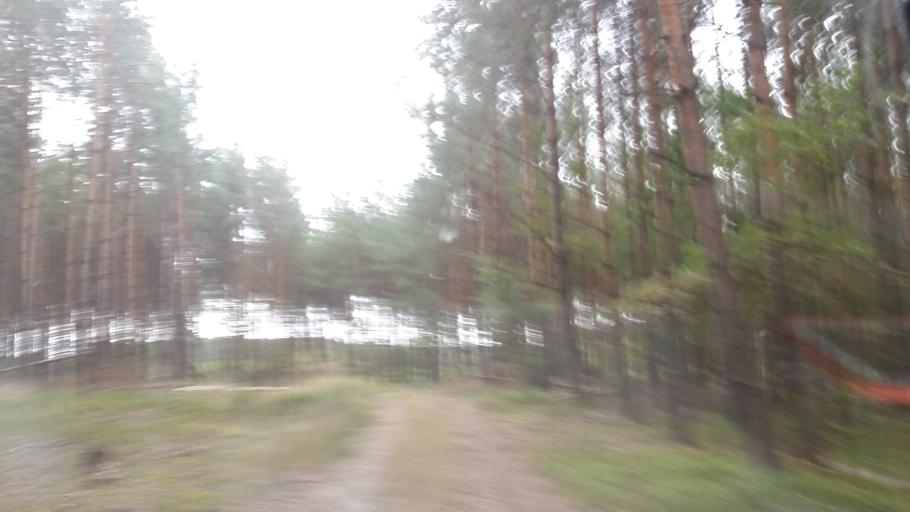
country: PL
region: West Pomeranian Voivodeship
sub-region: Powiat choszczenski
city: Bierzwnik
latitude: 52.9857
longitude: 15.6008
